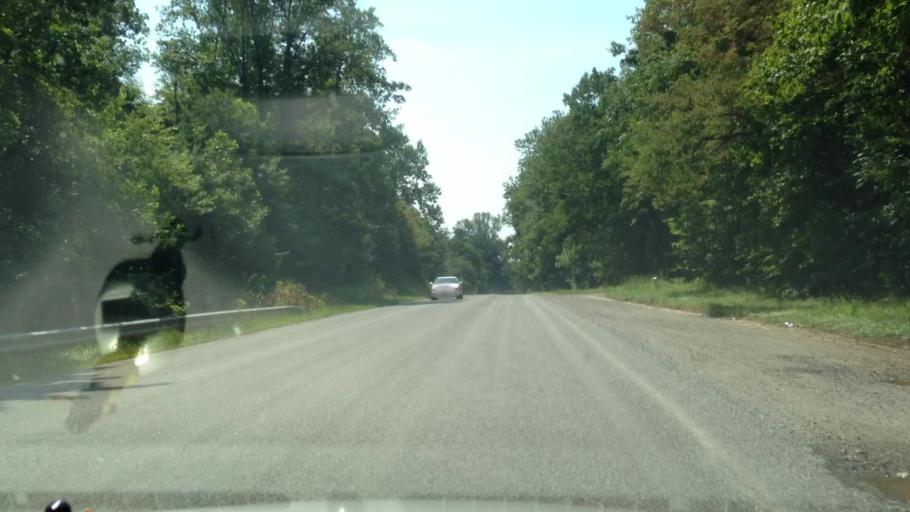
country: US
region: Virginia
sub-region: Patrick County
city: Stuart
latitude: 36.5969
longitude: -80.2959
